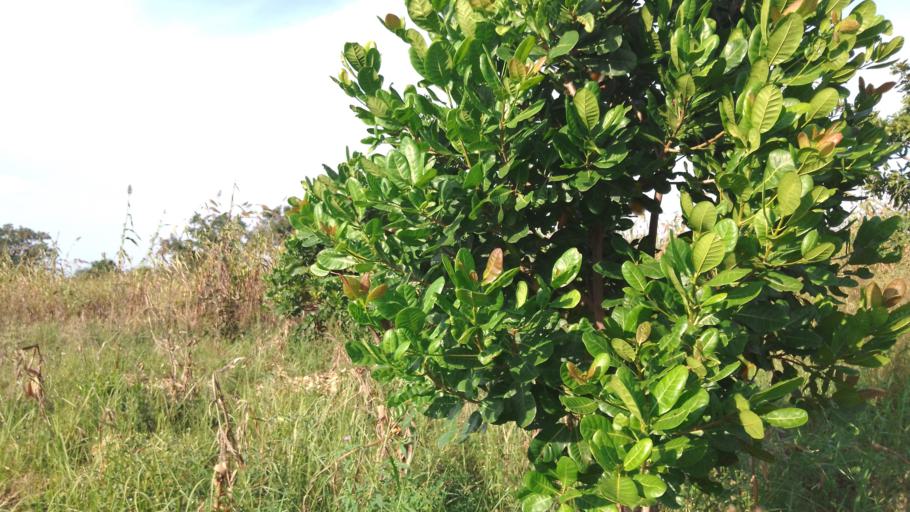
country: TG
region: Kara
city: Bafilo
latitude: 9.3919
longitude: 1.1459
